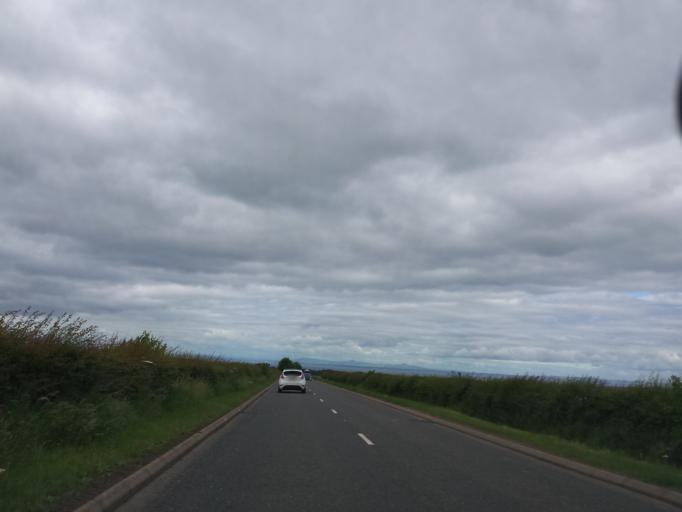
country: GB
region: Scotland
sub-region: East Lothian
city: Haddington
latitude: 55.9809
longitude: -2.8192
